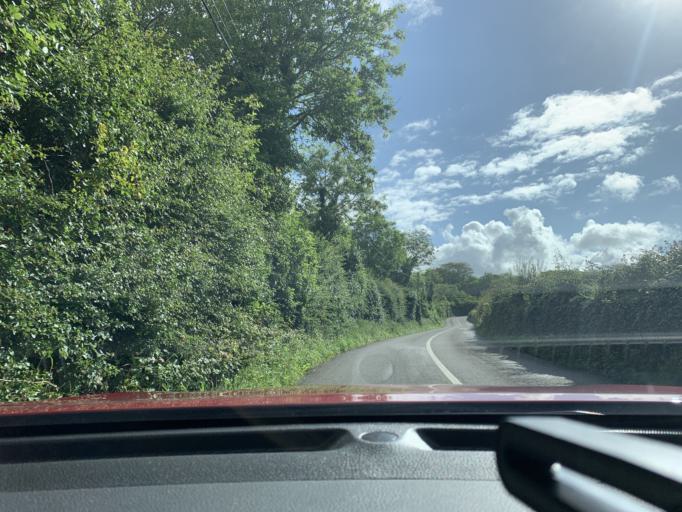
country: IE
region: Connaught
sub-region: Sligo
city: Strandhill
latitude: 54.3581
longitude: -8.5902
